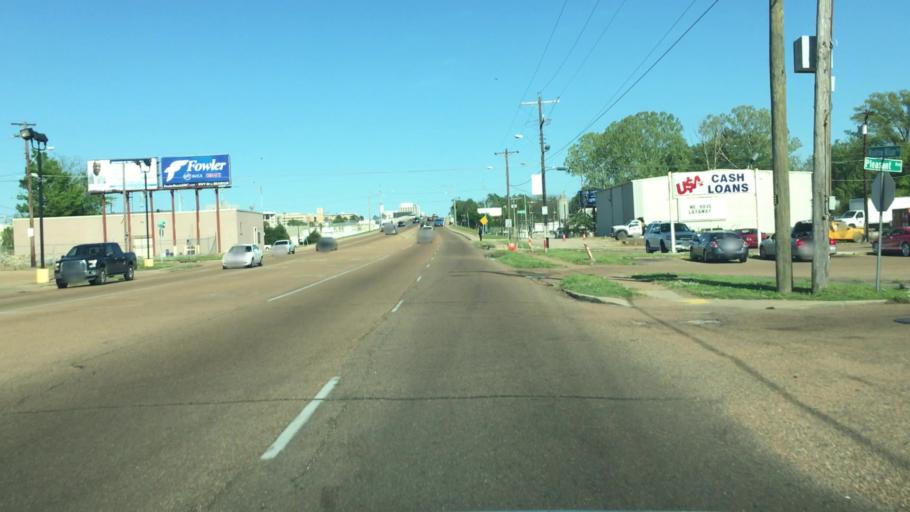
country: US
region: Mississippi
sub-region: Hinds County
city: Jackson
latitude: 32.3268
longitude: -90.1915
